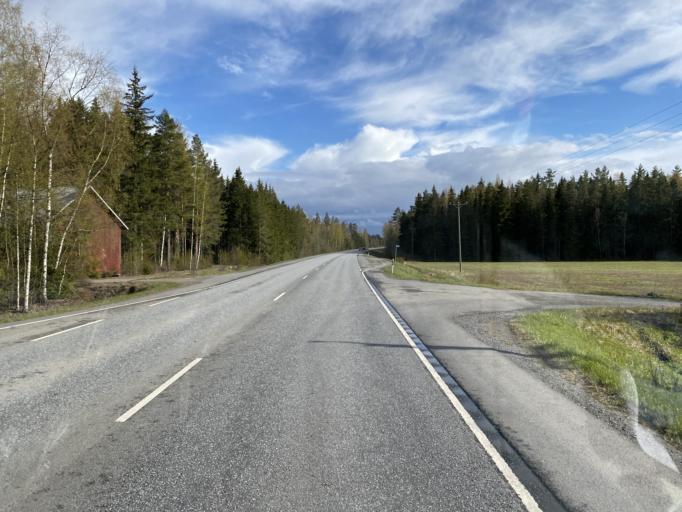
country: FI
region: Pirkanmaa
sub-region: Tampere
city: Lempaeaelae
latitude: 61.2780
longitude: 23.7462
